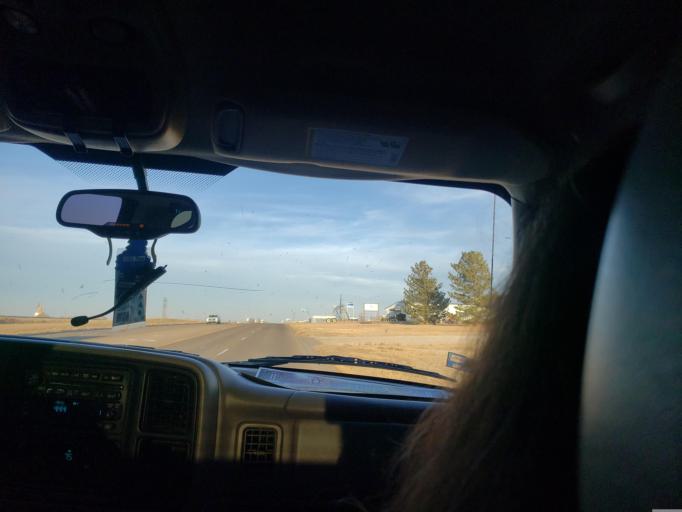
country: US
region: Oklahoma
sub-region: Texas County
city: Guymon
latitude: 36.6944
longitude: -101.4609
